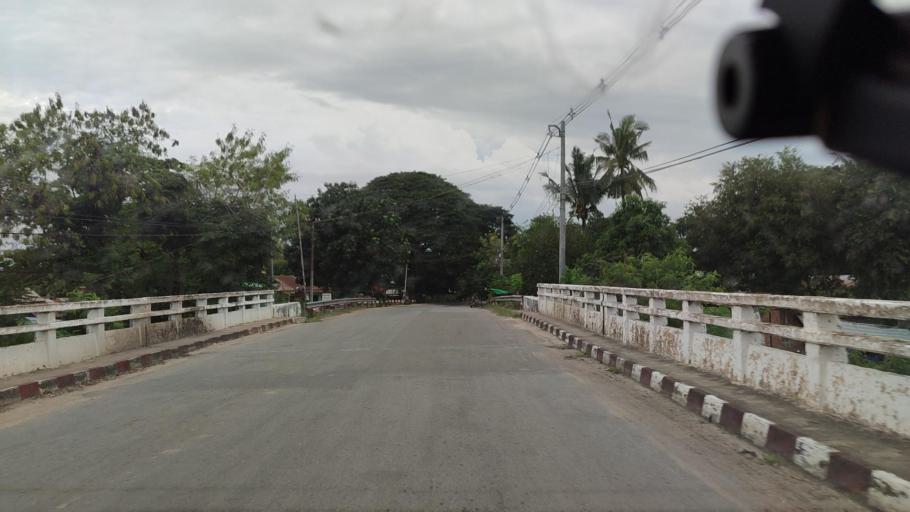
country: MM
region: Bago
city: Paungde
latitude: 18.5263
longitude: 95.3576
